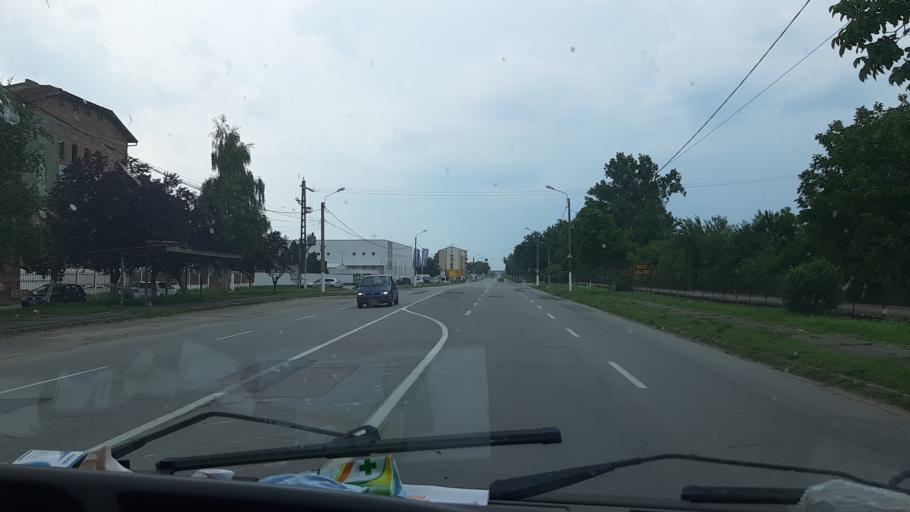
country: RO
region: Timis
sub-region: Municipiul Lugoj
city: Lugoj
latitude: 45.7058
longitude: 21.8895
